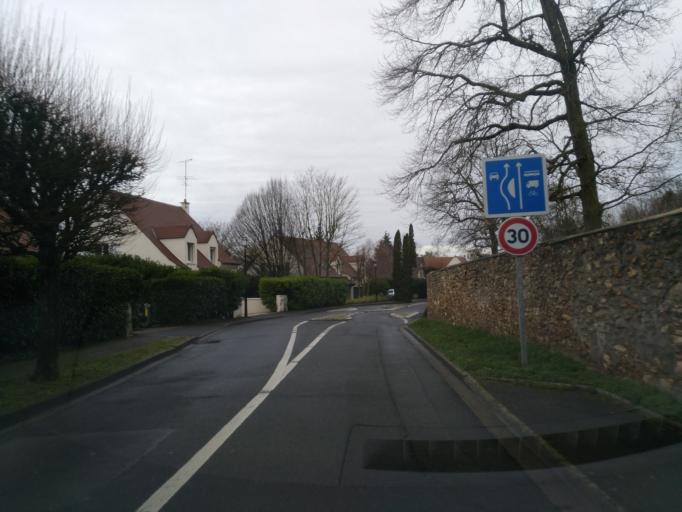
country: FR
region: Ile-de-France
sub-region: Departement des Yvelines
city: Saint-Nom-la-Breteche
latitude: 48.8651
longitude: 2.0247
